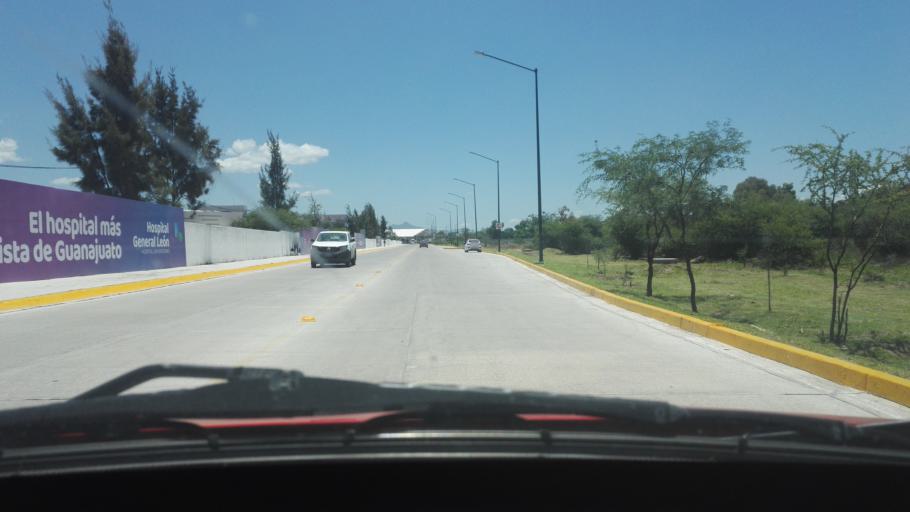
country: MX
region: Guanajuato
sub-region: Leon
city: Ladrilleras del Refugio
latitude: 21.0598
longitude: -101.5710
